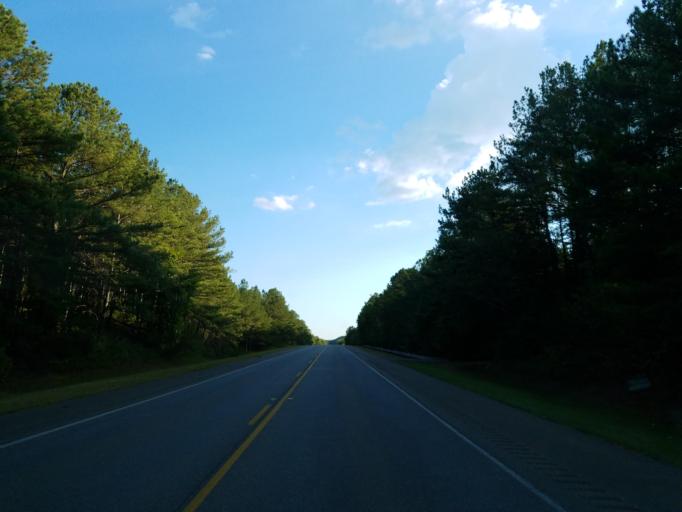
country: US
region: Georgia
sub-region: Murray County
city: Chatsworth
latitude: 34.6318
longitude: -84.7138
